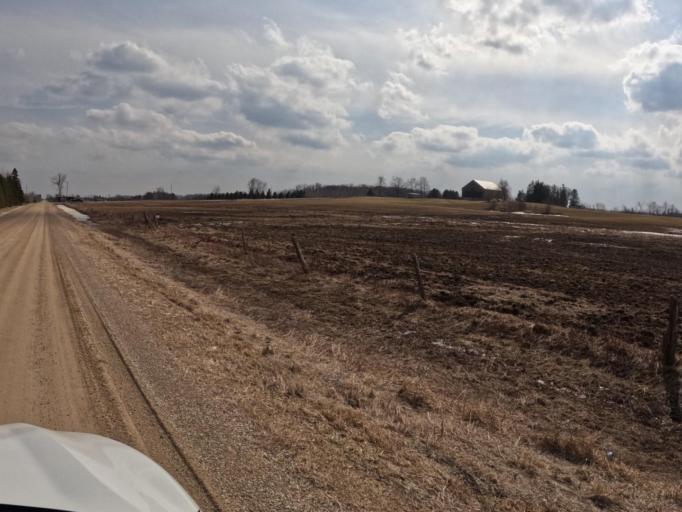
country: CA
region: Ontario
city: Shelburne
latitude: 43.9526
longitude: -80.3136
